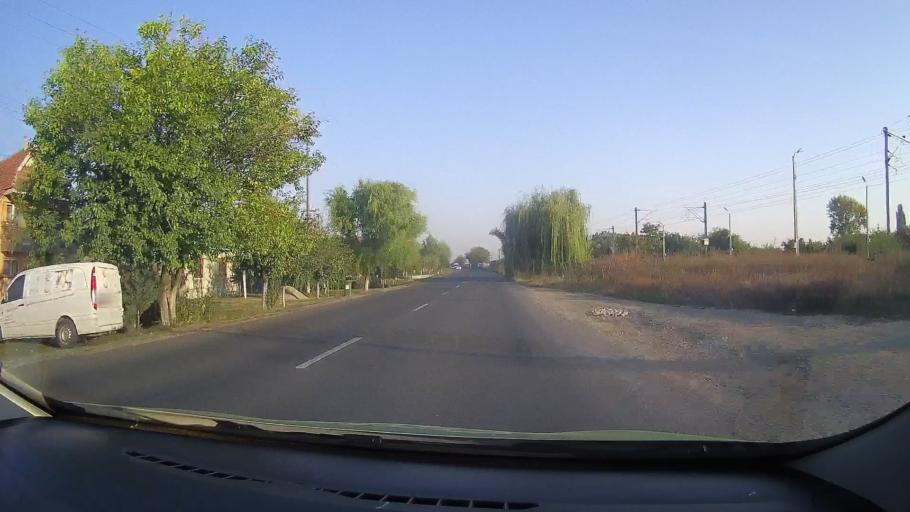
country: RO
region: Arad
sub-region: Comuna Sofronea
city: Sofronea
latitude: 46.2819
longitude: 21.3134
